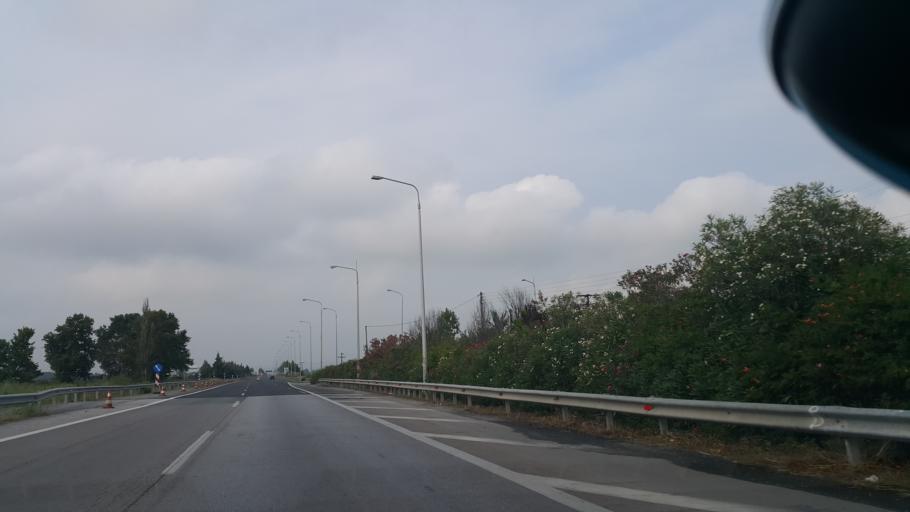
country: GR
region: Central Macedonia
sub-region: Nomos Imathias
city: Kleidi
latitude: 40.5557
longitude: 22.5985
